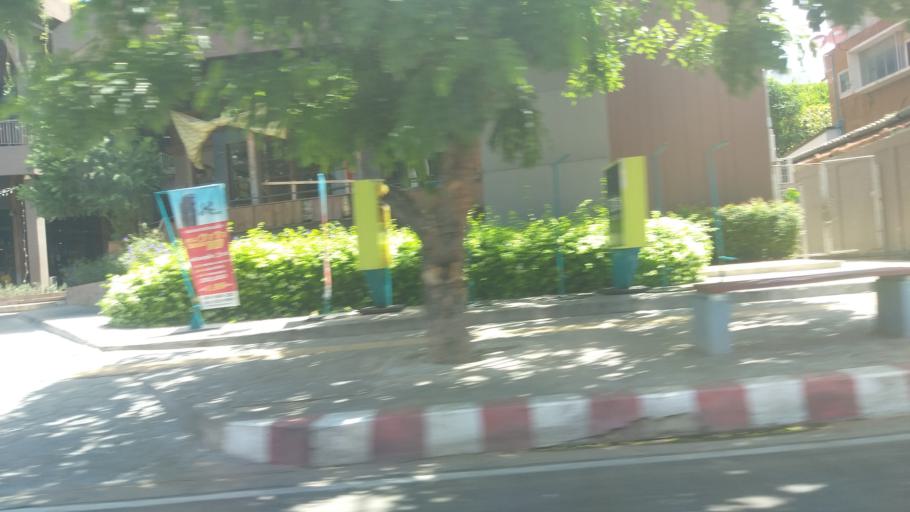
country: TH
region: Khon Kaen
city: Khon Kaen
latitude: 16.4311
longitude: 102.8308
